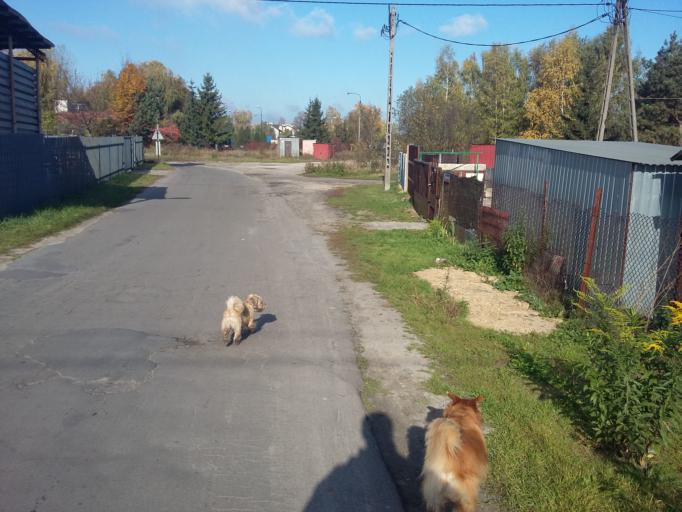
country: PL
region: Lodz Voivodeship
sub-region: Powiat pabianicki
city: Ksawerow
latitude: 51.7331
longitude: 19.3819
